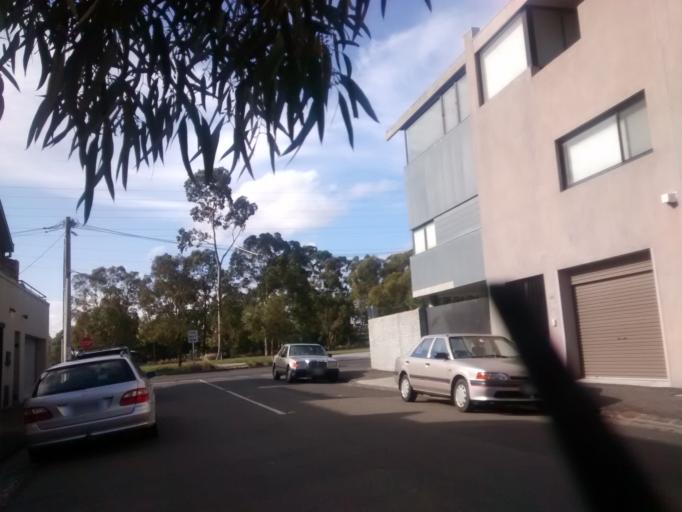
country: AU
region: Victoria
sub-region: Yarra
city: North Fitzroy
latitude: -37.7814
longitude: 144.9842
